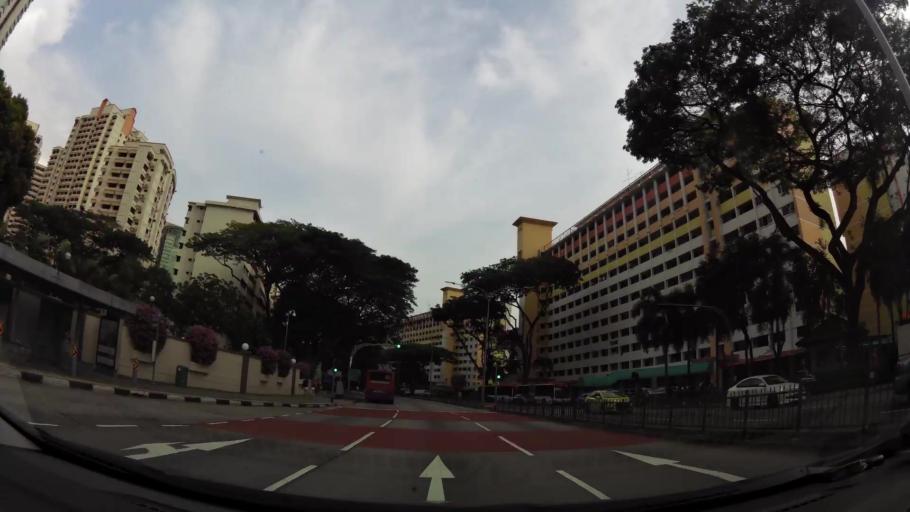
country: SG
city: Singapore
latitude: 1.3327
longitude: 103.8440
